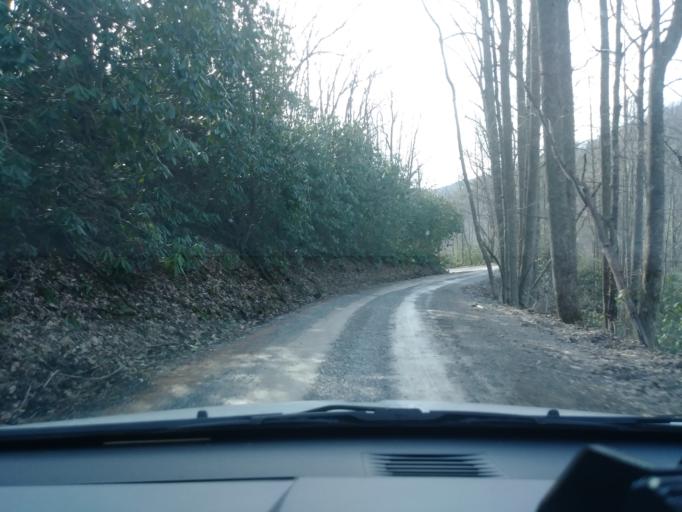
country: US
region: Tennessee
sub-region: Greene County
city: Tusculum
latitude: 36.0280
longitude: -82.7270
